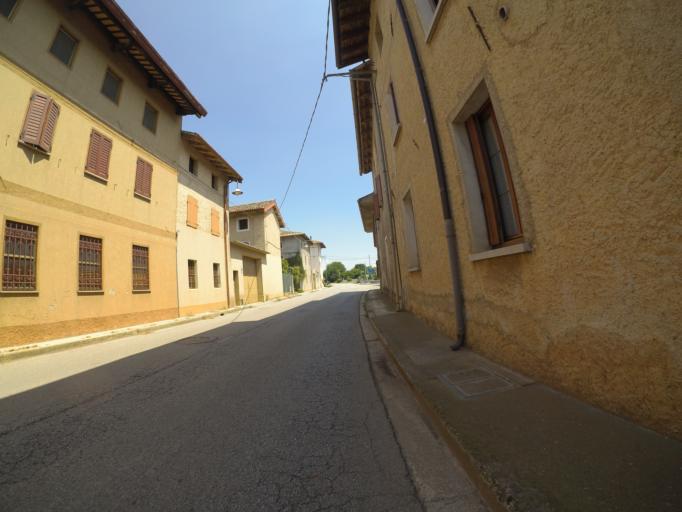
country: IT
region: Friuli Venezia Giulia
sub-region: Provincia di Udine
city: Bertiolo
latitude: 45.9712
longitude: 13.0696
